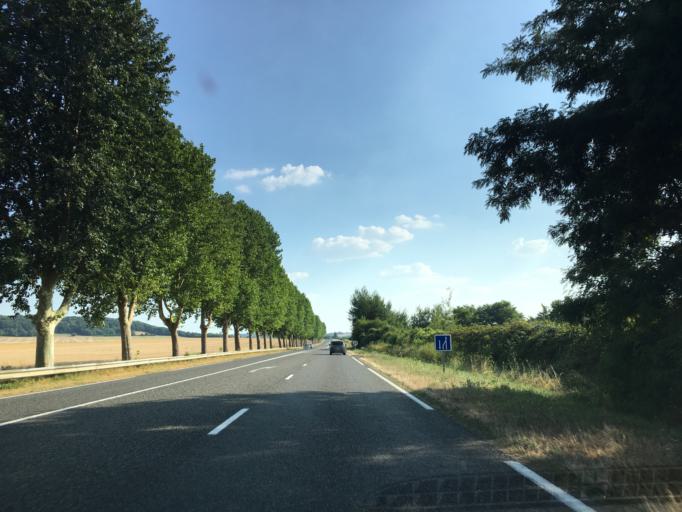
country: FR
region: Bourgogne
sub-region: Departement de l'Yonne
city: Veron
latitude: 48.1186
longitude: 3.2907
